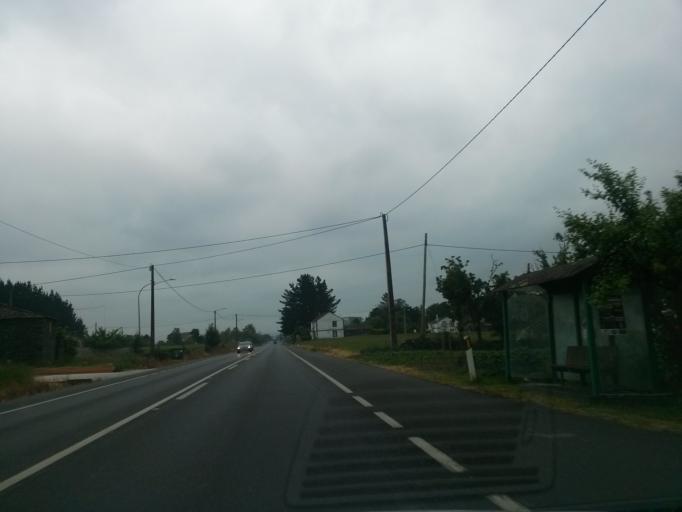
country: ES
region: Galicia
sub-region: Provincia de Lugo
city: Rabade
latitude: 43.1316
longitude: -7.6512
